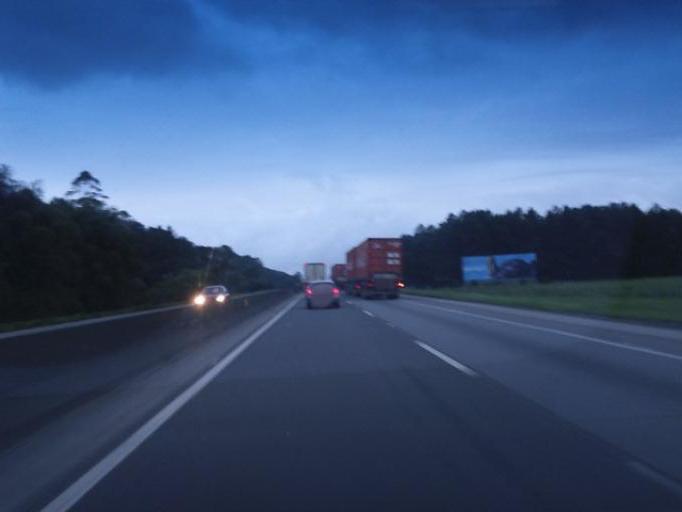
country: BR
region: Santa Catarina
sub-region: Barra Velha
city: Barra Velha
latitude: -26.5029
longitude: -48.7282
